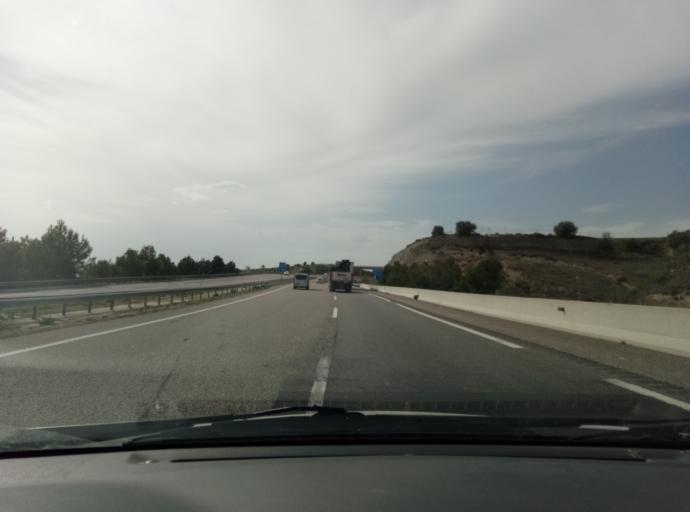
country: ES
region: Catalonia
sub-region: Provincia de Lleida
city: Cervera
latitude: 41.6662
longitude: 1.2992
